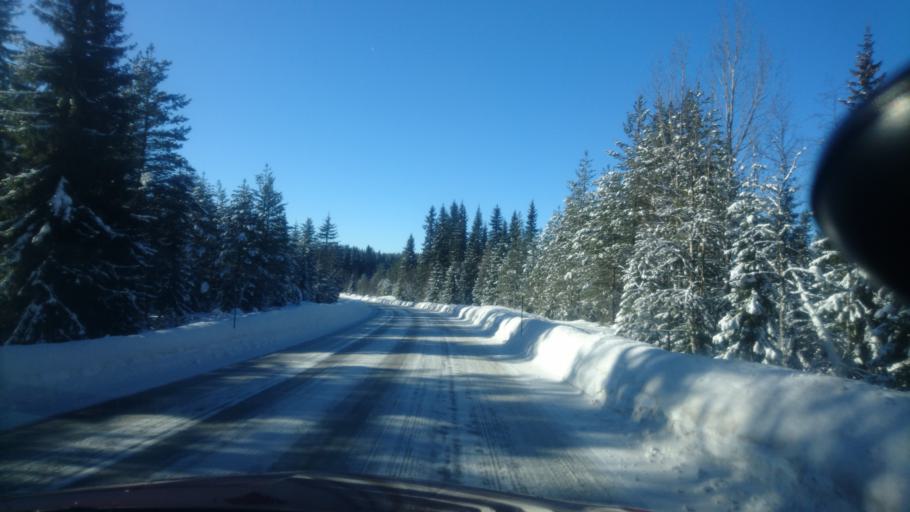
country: NO
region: Hedmark
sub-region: Trysil
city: Innbygda
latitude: 61.2718
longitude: 12.4661
